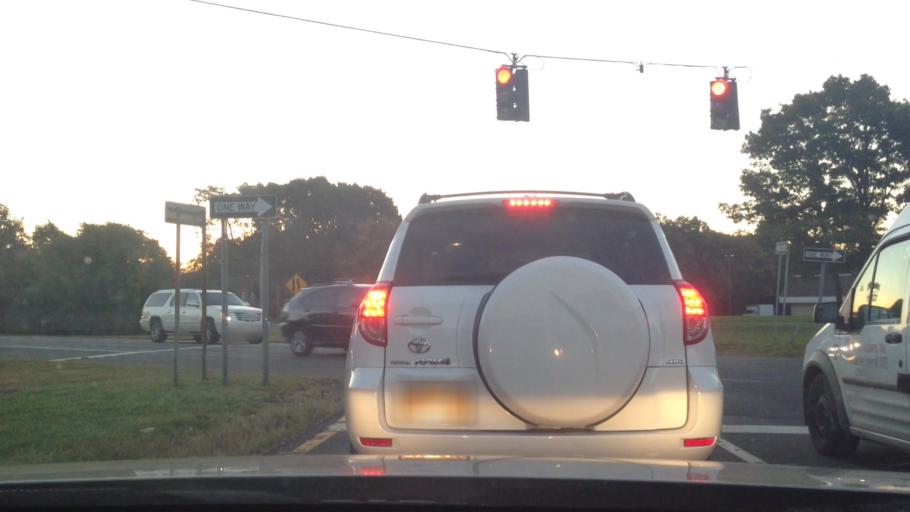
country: US
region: New York
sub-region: Suffolk County
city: Mount Sinai
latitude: 40.9326
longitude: -73.0328
